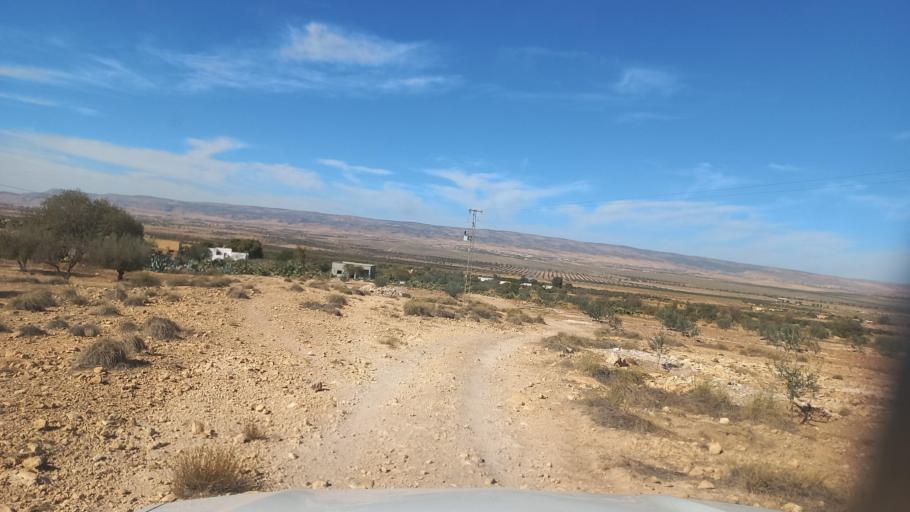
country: TN
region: Al Qasrayn
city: Kasserine
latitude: 35.2004
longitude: 8.9723
